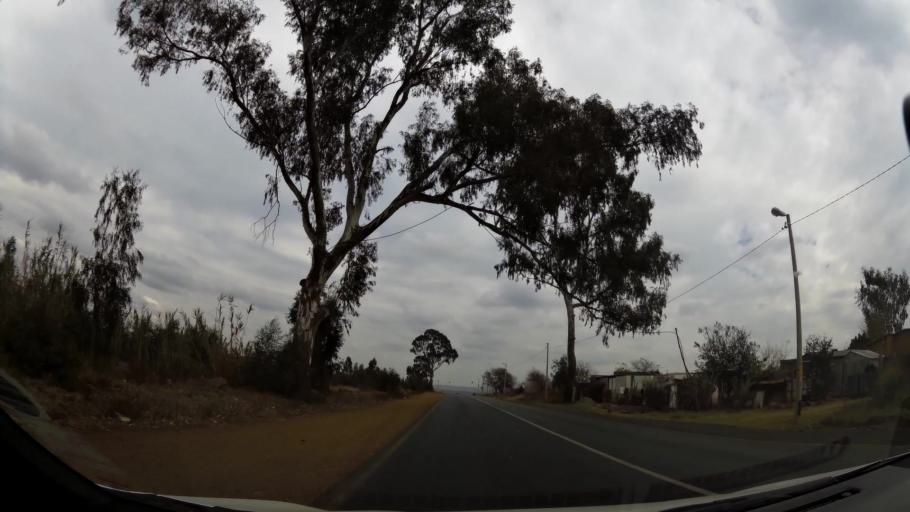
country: ZA
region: Gauteng
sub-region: Ekurhuleni Metropolitan Municipality
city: Germiston
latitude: -26.3736
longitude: 28.1092
